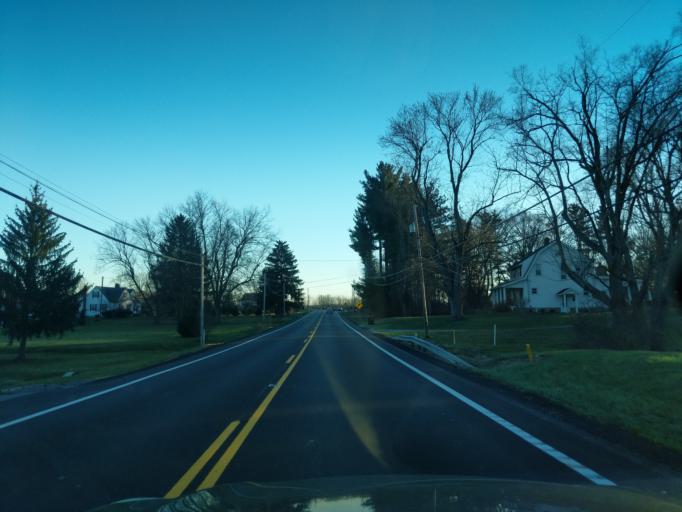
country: US
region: Ohio
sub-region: Licking County
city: Heath
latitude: 40.0030
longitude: -82.4047
